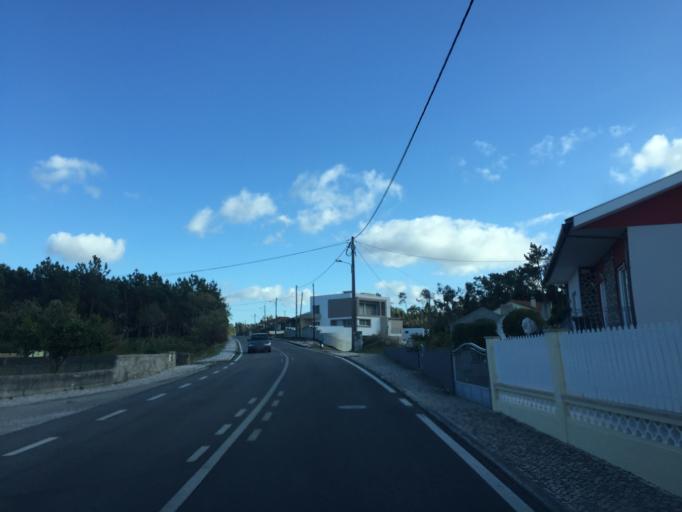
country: PT
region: Coimbra
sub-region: Figueira da Foz
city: Tavarede
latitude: 40.2111
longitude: -8.8466
